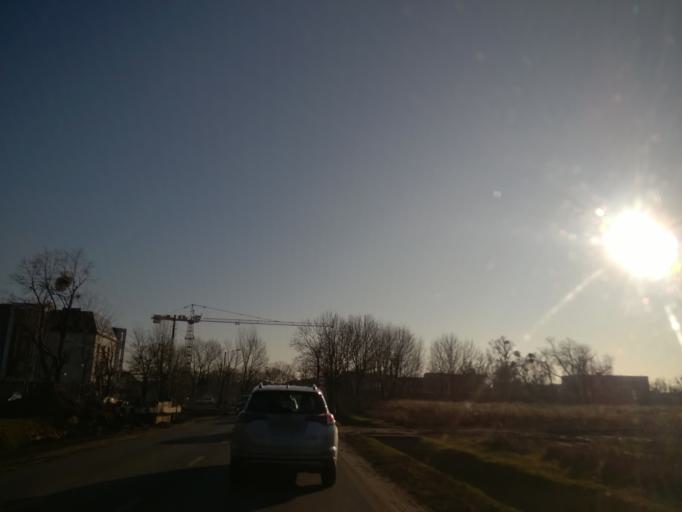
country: PL
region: Lower Silesian Voivodeship
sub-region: Powiat wroclawski
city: Bielany Wroclawskie
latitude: 51.0805
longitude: 16.9568
